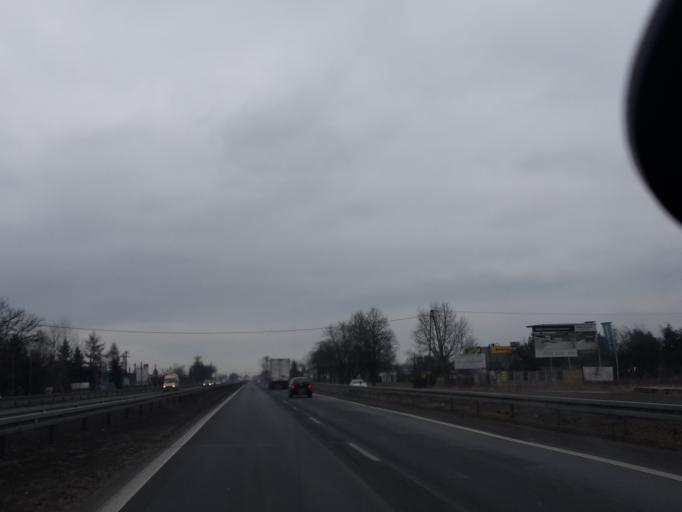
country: PL
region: Masovian Voivodeship
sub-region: Powiat warszawski zachodni
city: Dziekanow Lesny
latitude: 52.3620
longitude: 20.8215
